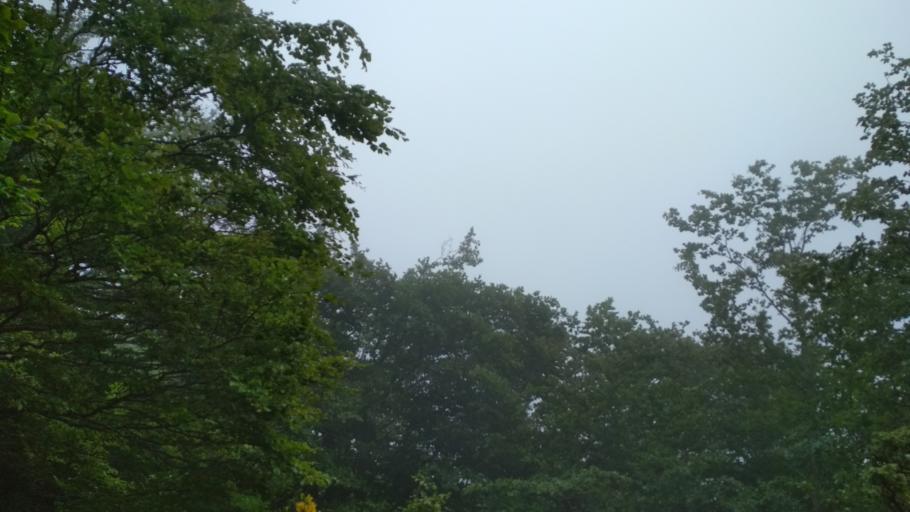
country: ES
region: Catalonia
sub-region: Provincia de Barcelona
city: Fogars de Montclus
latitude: 41.7806
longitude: 2.4346
